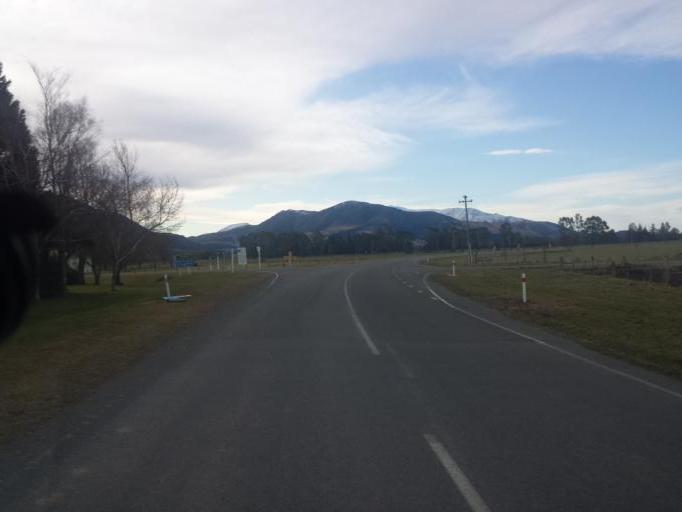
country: NZ
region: Canterbury
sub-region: Ashburton District
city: Methven
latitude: -43.6537
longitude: 171.4428
